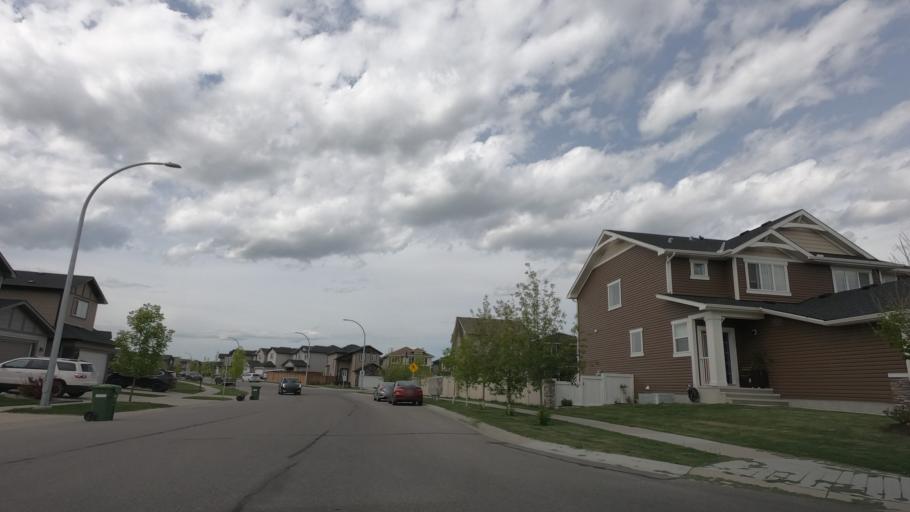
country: CA
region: Alberta
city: Airdrie
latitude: 51.2730
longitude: -114.0425
